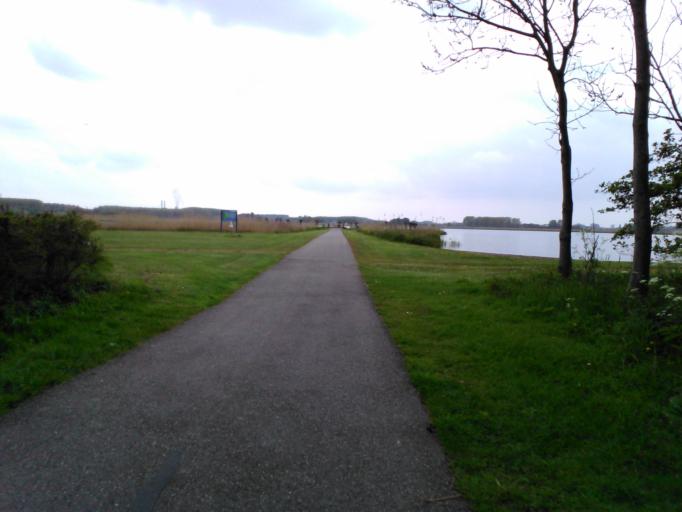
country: NL
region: South Holland
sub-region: Gemeente Vlaardingen
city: Vlaardingen
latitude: 51.9167
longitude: 4.3042
